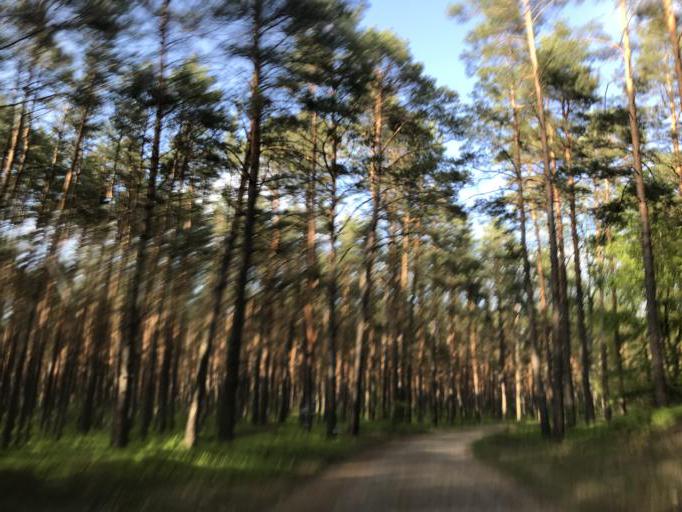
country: DE
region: Brandenburg
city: Joachimsthal
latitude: 52.9583
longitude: 13.6759
